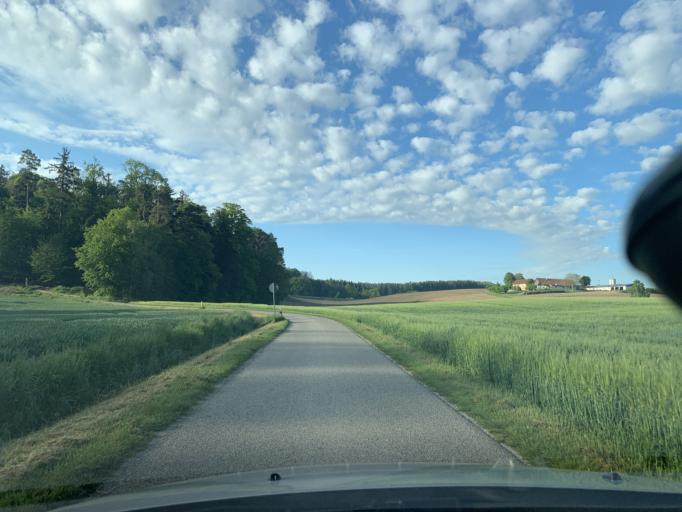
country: DE
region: Bavaria
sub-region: Lower Bavaria
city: Stallwang
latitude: 48.5209
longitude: 12.2121
